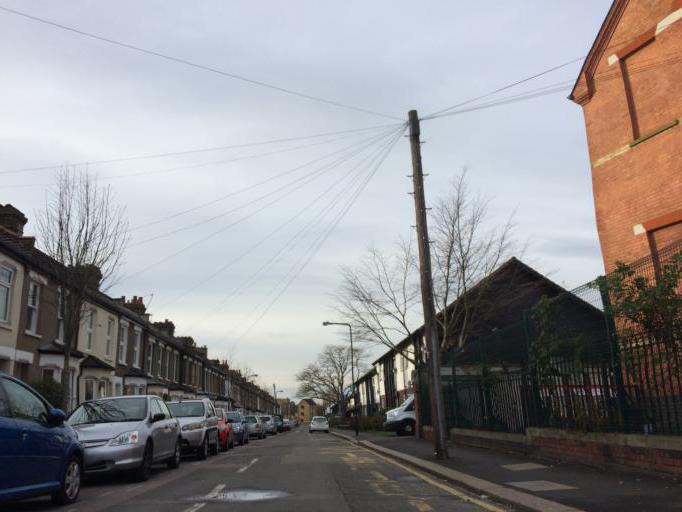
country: GB
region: England
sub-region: Greater London
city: Walthamstow
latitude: 51.5813
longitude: -0.0244
